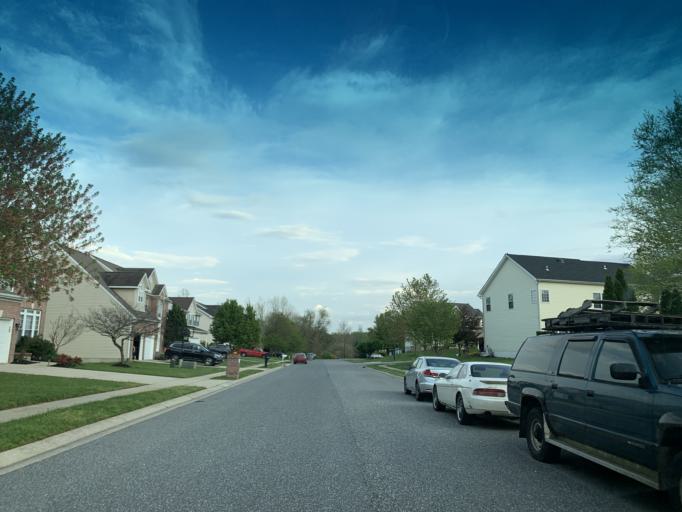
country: US
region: Maryland
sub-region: Harford County
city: Bel Air South
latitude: 39.5081
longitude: -76.3413
